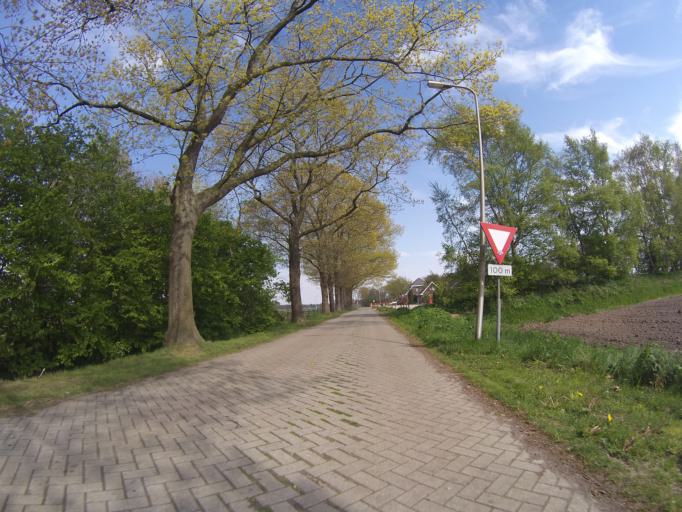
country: DE
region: Lower Saxony
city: Emlichheim
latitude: 52.6571
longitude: 6.8145
